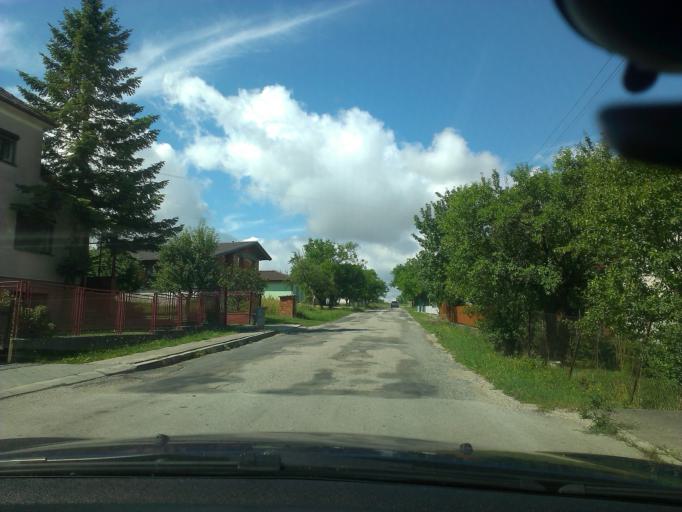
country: SK
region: Trenciansky
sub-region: Okres Myjava
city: Myjava
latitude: 48.7720
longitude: 17.5909
